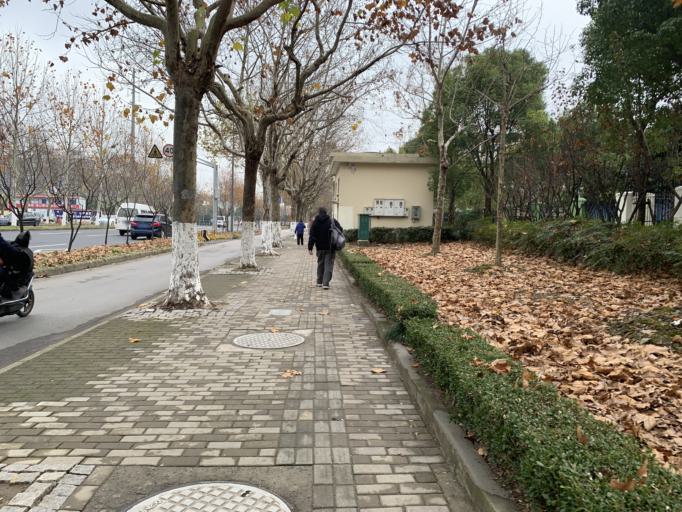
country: CN
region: Shanghai Shi
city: Huamu
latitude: 31.1921
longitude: 121.5351
